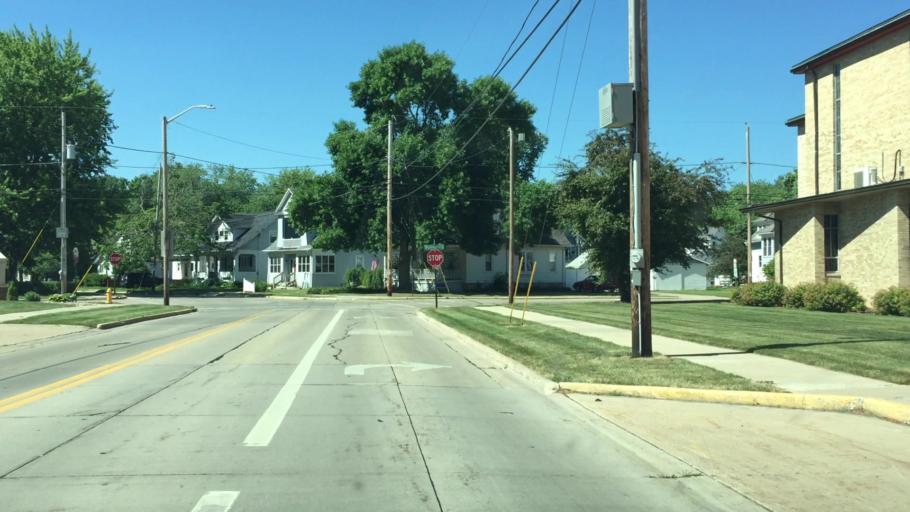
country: US
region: Wisconsin
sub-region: Winnebago County
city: Neenah
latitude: 44.1820
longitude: -88.4597
